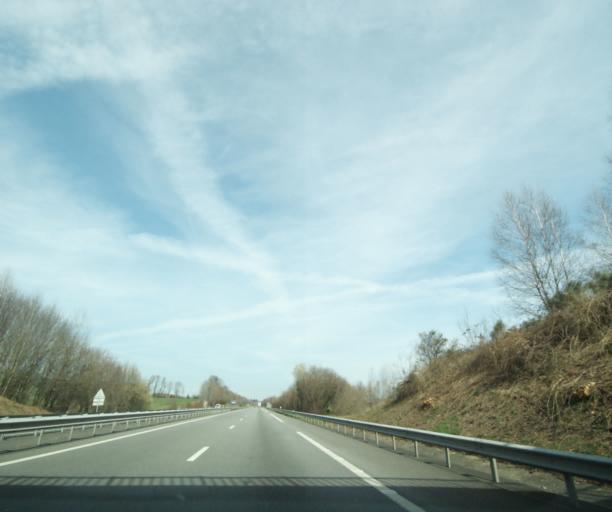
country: FR
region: Limousin
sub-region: Departement de la Correze
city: Uzerche
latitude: 45.4432
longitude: 1.5103
